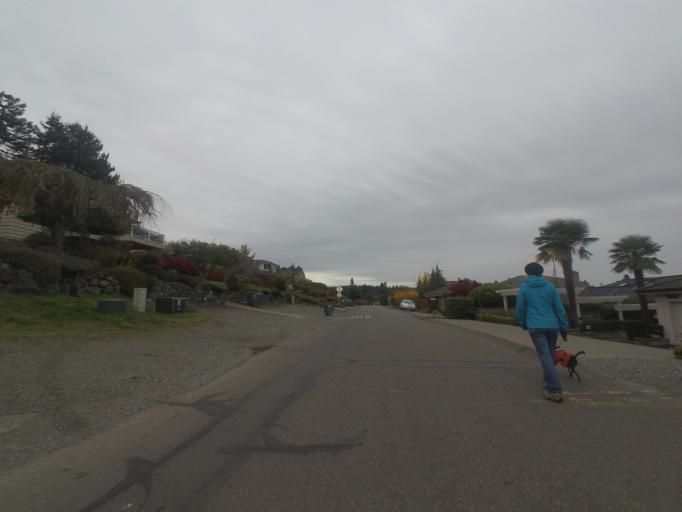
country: US
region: Washington
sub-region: Pierce County
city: University Place
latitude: 47.2266
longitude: -122.5609
